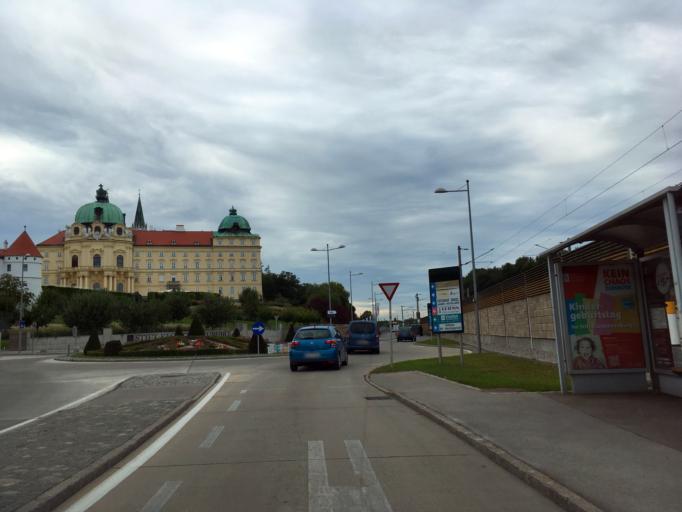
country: AT
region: Lower Austria
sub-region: Politischer Bezirk Wien-Umgebung
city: Klosterneuburg
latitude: 48.3048
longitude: 16.3300
